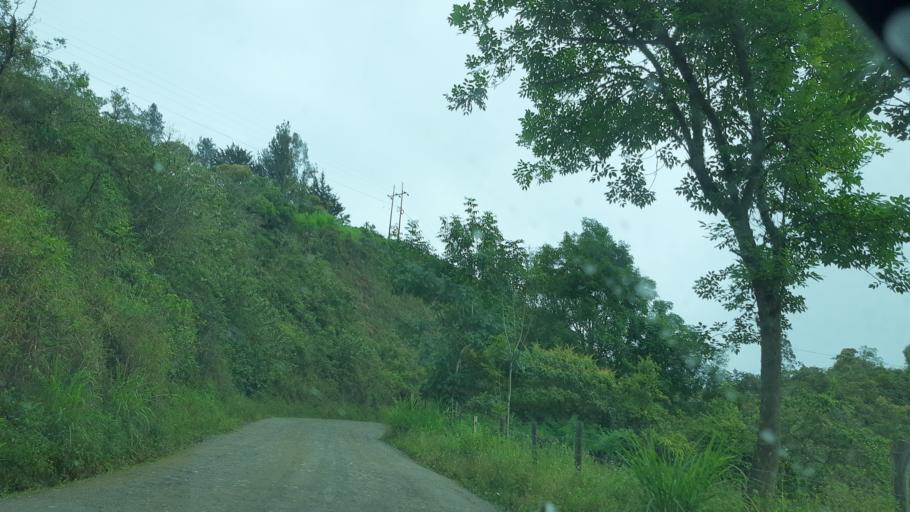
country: CO
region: Cundinamarca
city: Tenza
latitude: 5.0363
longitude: -73.4371
